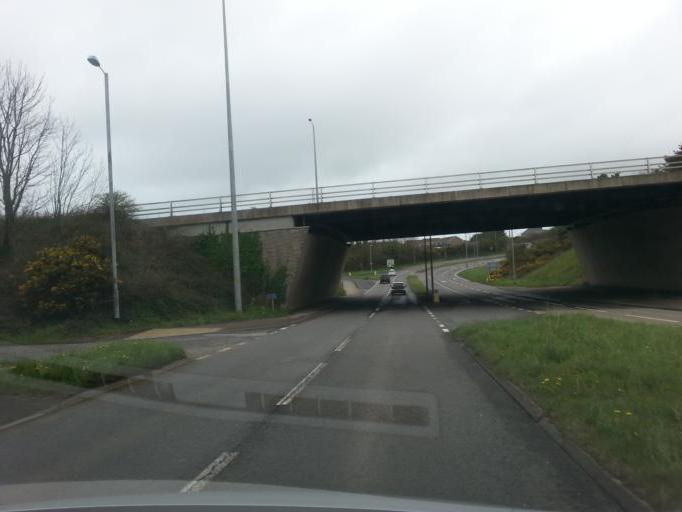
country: GB
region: England
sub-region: Cornwall
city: Camborne
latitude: 50.2283
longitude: -5.2832
